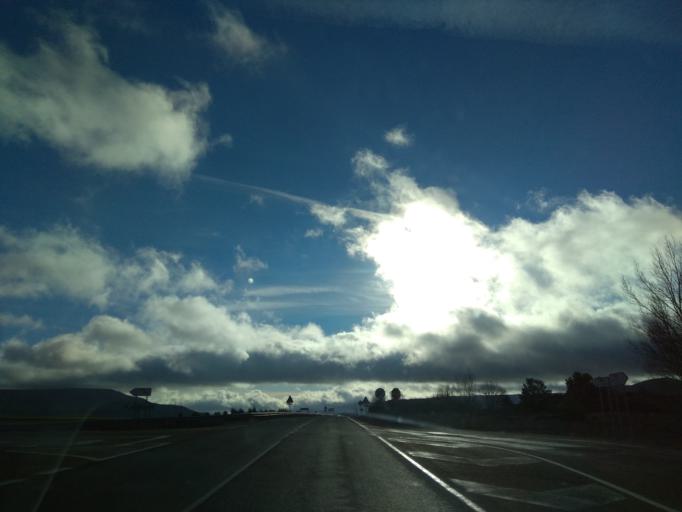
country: ES
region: Castille and Leon
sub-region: Provincia de Palencia
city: Pomar de Valdivia
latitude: 42.7716
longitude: -4.1980
